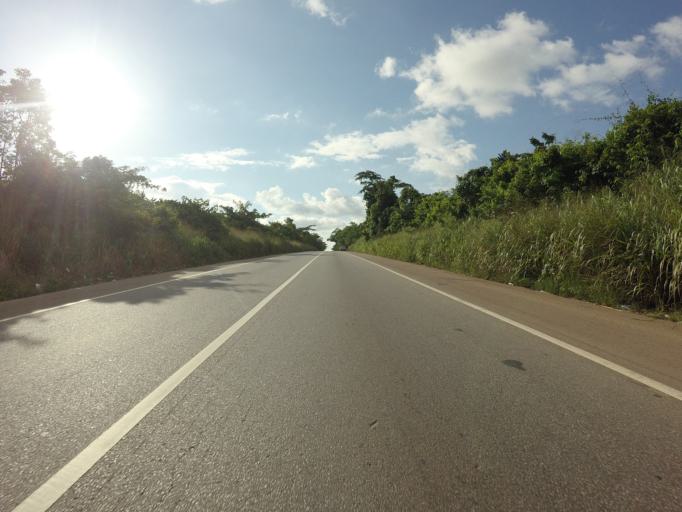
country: GH
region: Ashanti
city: Tafo
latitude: 6.8883
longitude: -1.6470
